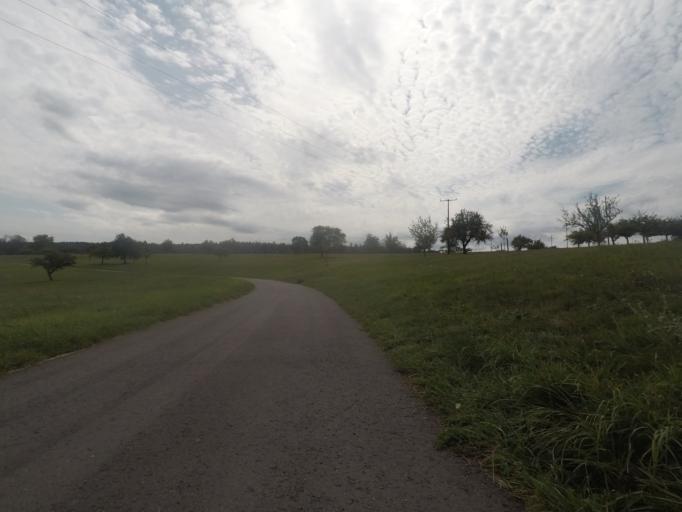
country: DE
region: Baden-Wuerttemberg
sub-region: Karlsruhe Region
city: Bad Herrenalb
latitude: 48.8399
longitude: 8.4524
